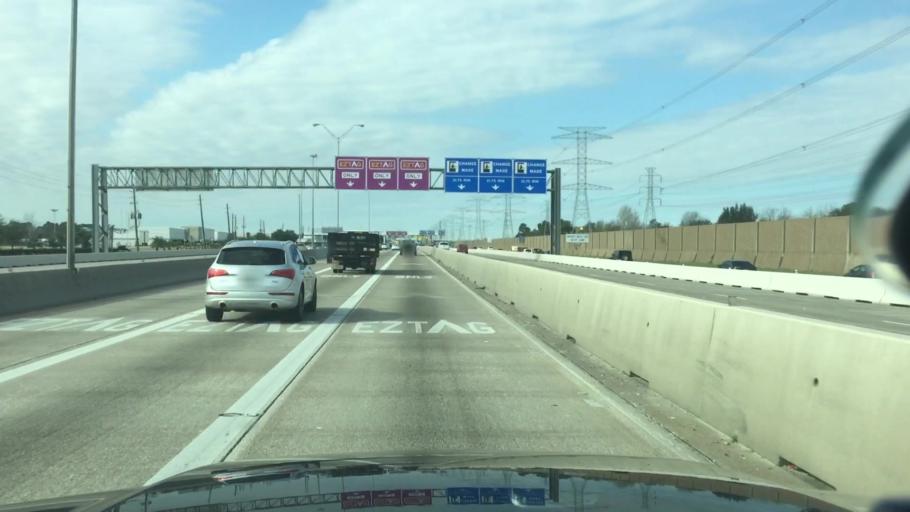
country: US
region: Texas
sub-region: Harris County
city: Hudson
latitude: 29.9378
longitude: -95.4668
